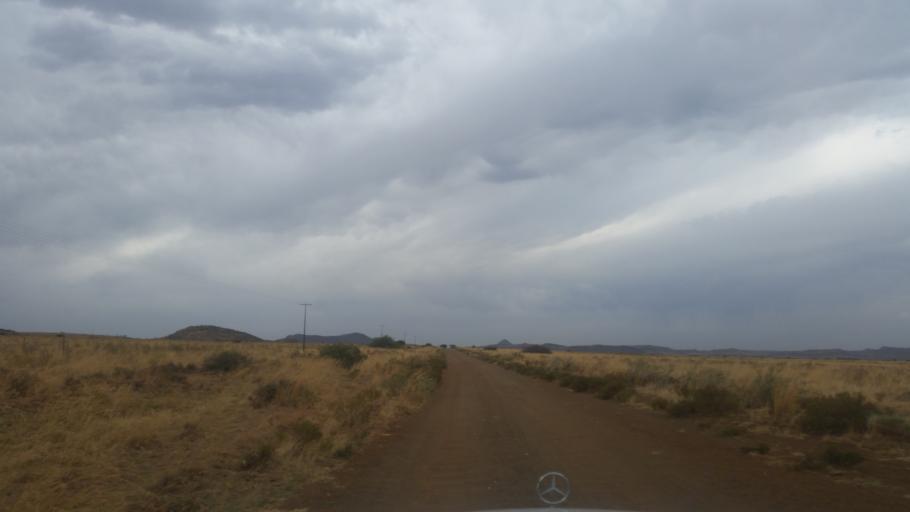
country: ZA
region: Orange Free State
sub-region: Xhariep District Municipality
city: Trompsburg
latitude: -30.5056
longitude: 25.9432
